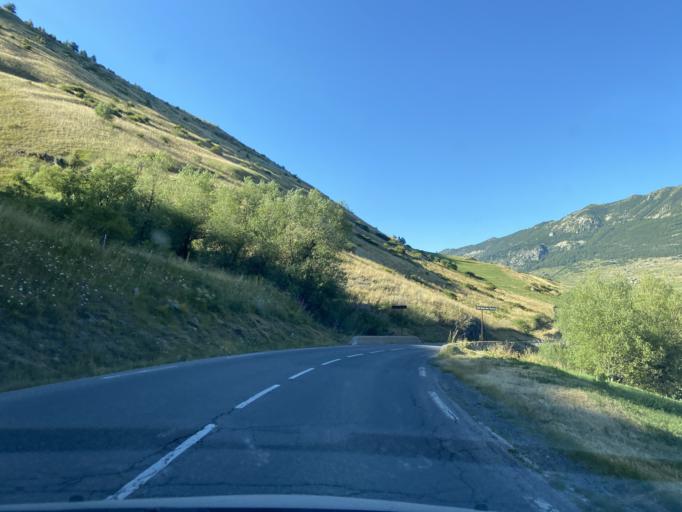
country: FR
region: Provence-Alpes-Cote d'Azur
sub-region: Departement des Hautes-Alpes
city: Guillestre
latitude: 44.5830
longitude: 6.6830
